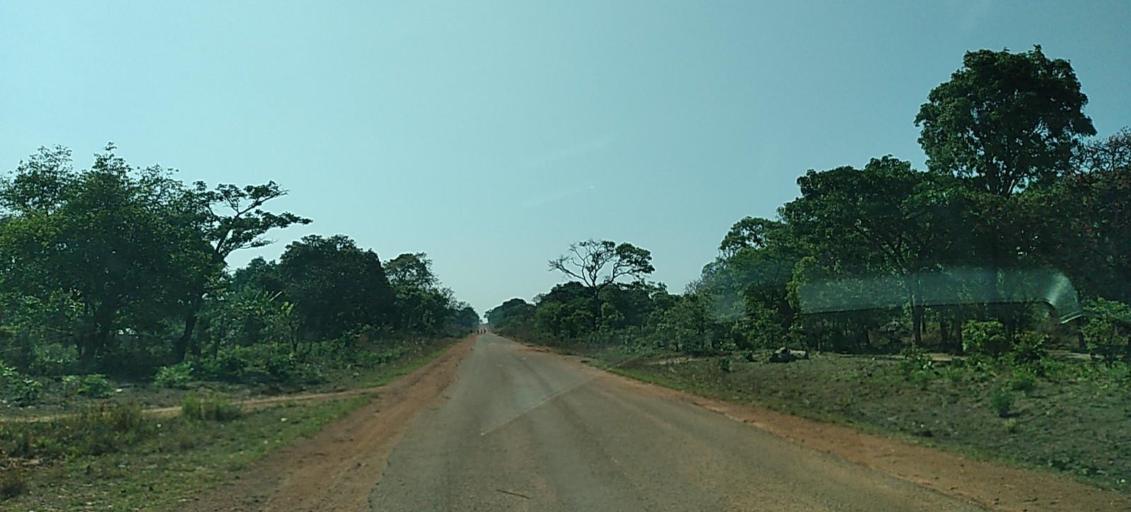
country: ZM
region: North-Western
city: Mwinilunga
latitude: -11.9009
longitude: 25.2790
